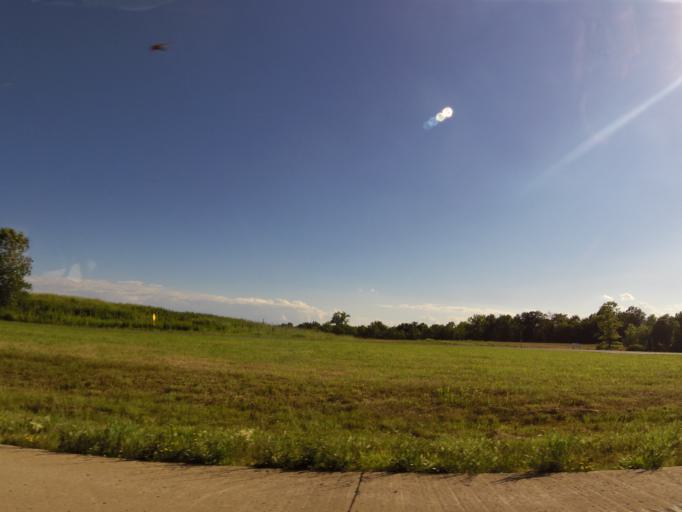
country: US
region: Missouri
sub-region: Ralls County
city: New London
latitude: 39.5378
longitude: -91.3643
